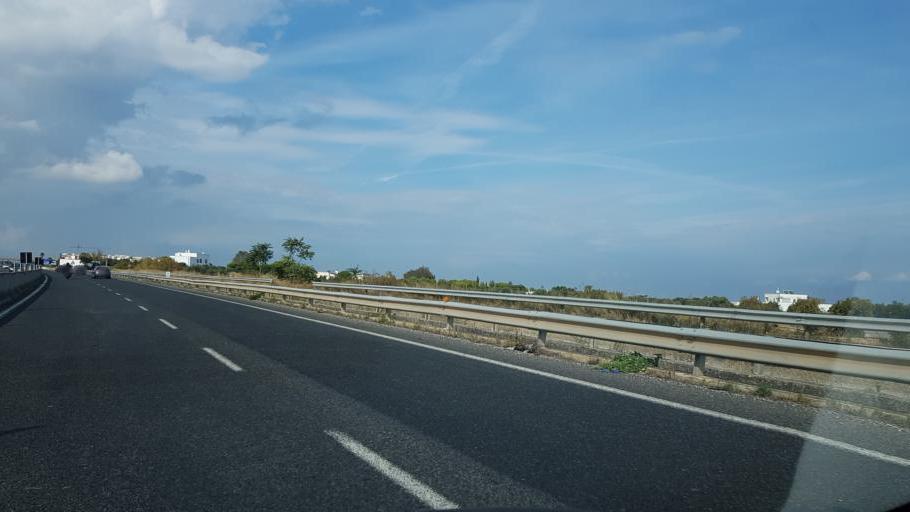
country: IT
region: Apulia
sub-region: Provincia di Bari
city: Monopoli
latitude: 40.9256
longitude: 17.3115
